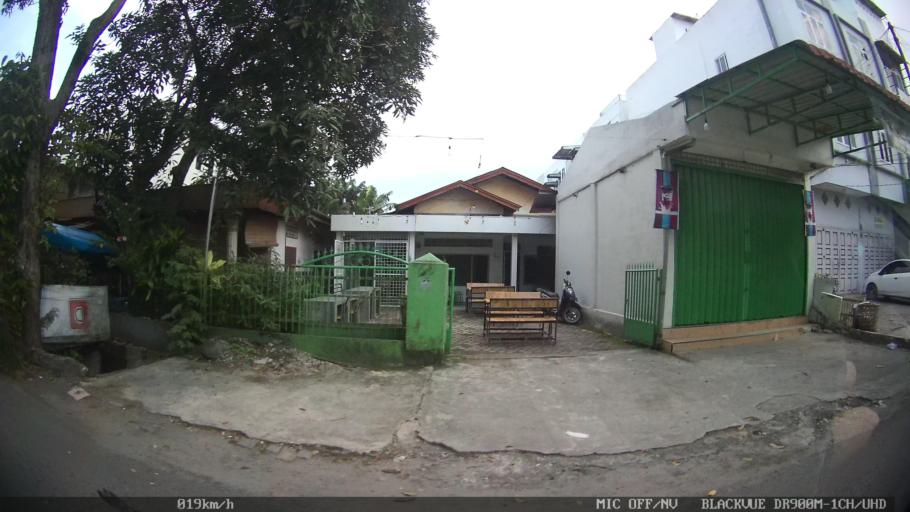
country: ID
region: North Sumatra
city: Medan
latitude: 3.6094
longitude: 98.6978
